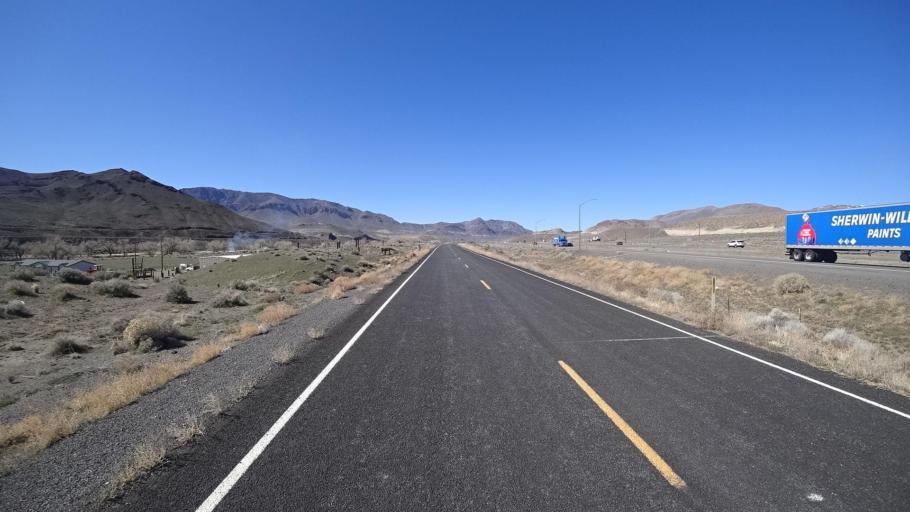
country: US
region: Nevada
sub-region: Lyon County
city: Fernley
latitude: 39.6044
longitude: -119.3284
